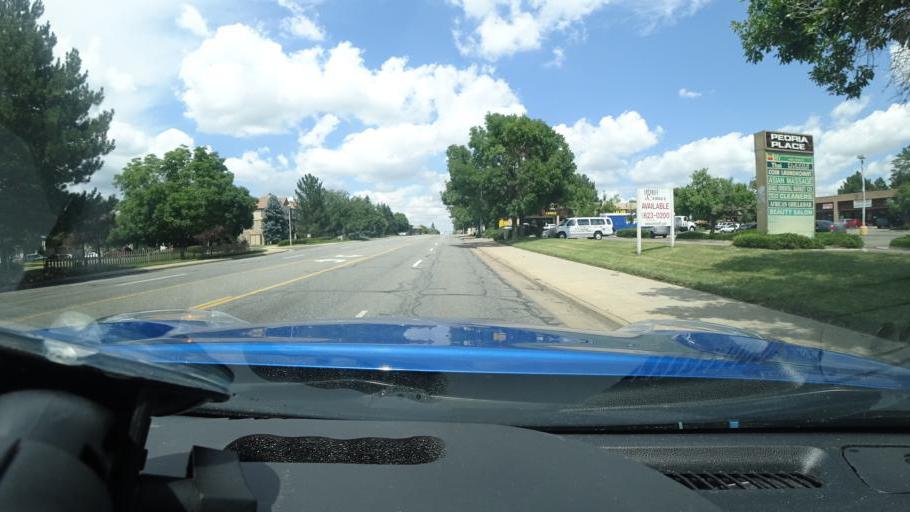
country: US
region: Colorado
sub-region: Adams County
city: Aurora
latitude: 39.6989
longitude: -104.8470
